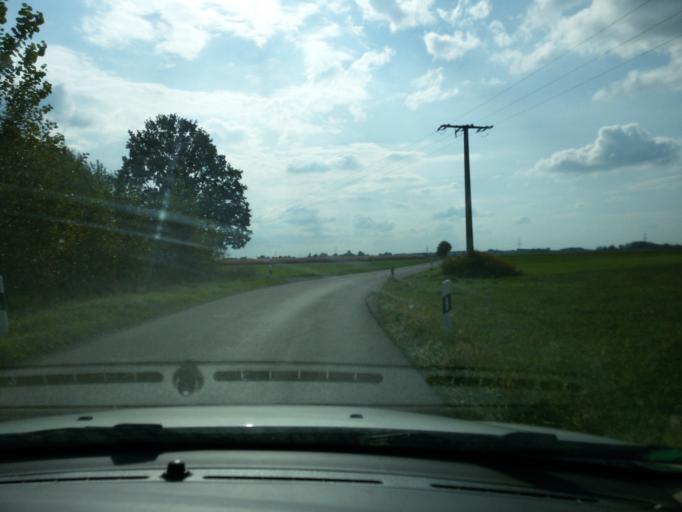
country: DE
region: Bavaria
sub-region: Swabia
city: Lamerdingen
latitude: 48.0615
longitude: 10.7875
